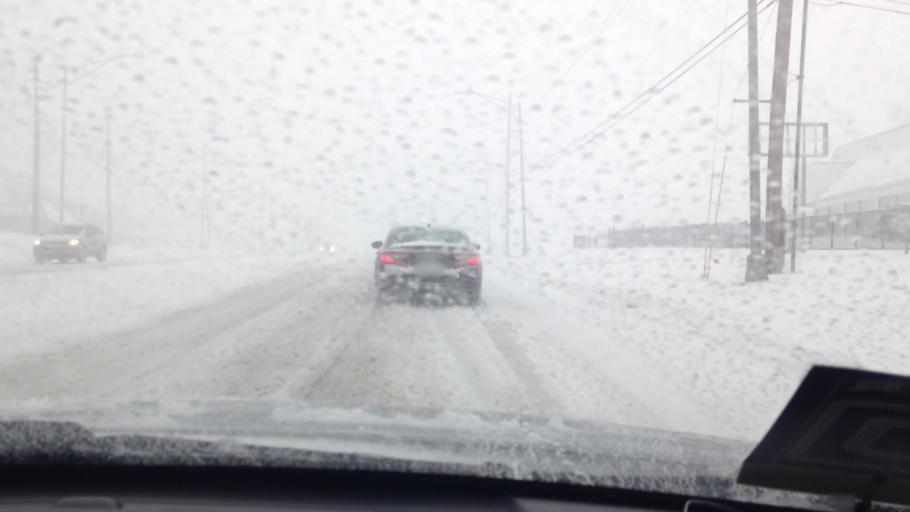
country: US
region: Kansas
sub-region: Wyandotte County
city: Kansas City
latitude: 39.1166
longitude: -94.6957
